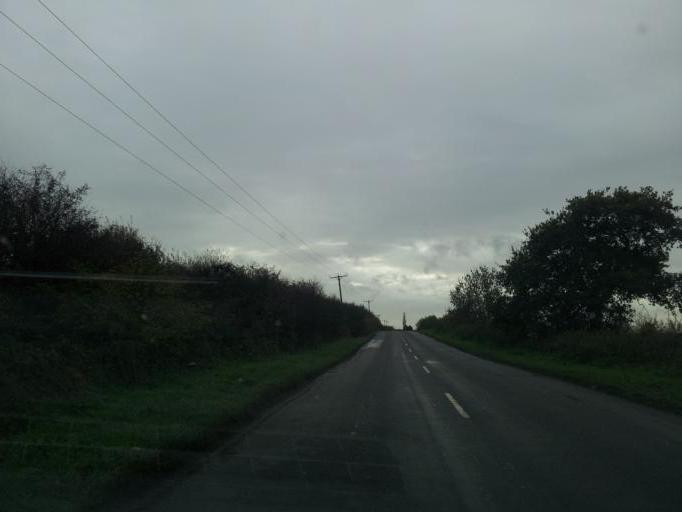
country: GB
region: England
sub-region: Nottinghamshire
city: Newark on Trent
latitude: 53.0382
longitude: -0.7978
